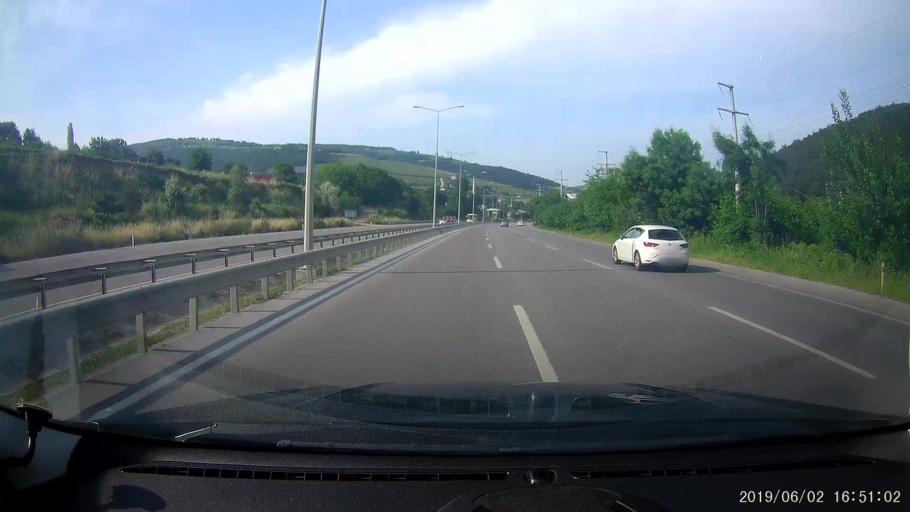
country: TR
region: Samsun
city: Taflan
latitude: 41.2671
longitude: 36.1774
